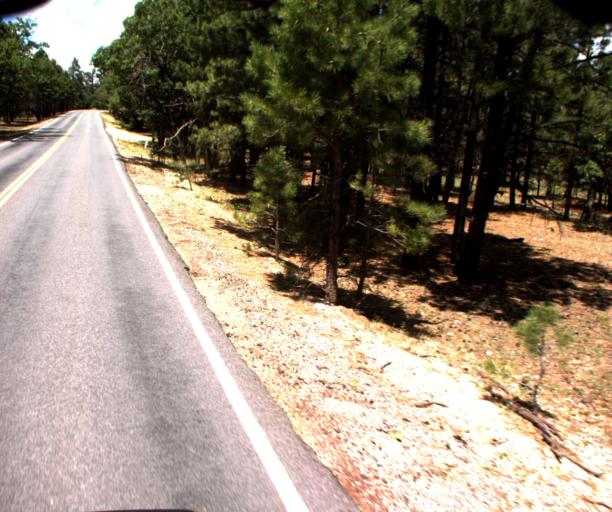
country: US
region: Arizona
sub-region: Coconino County
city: Grand Canyon
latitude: 35.9712
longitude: -111.9799
